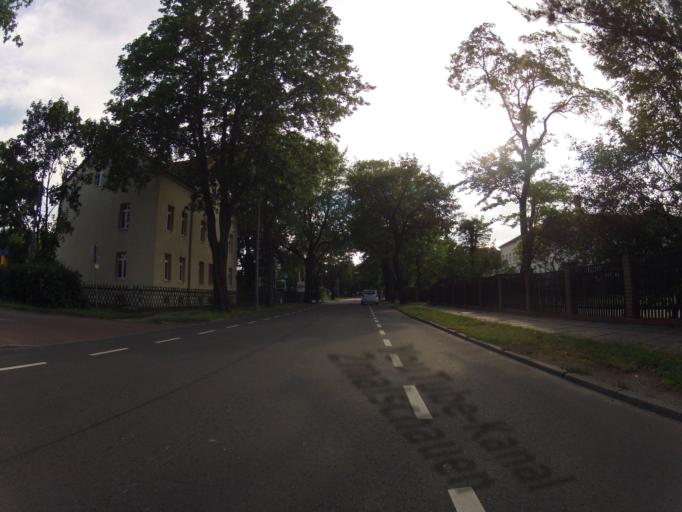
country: DE
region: Saxony
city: Taucha
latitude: 51.3469
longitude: 12.4925
